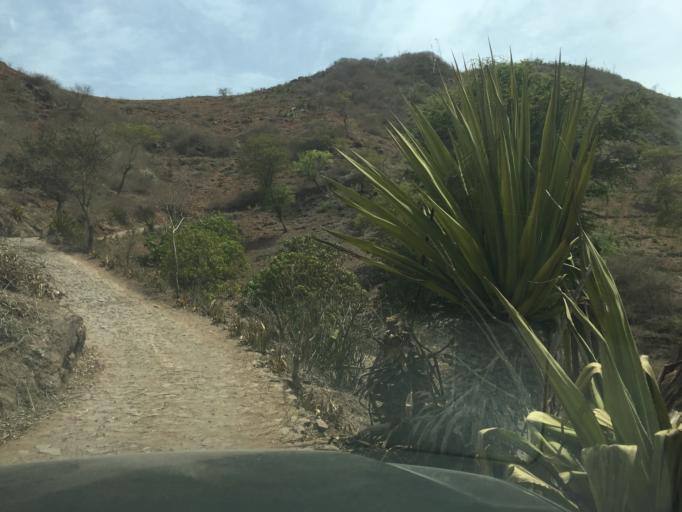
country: CV
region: Sao Salvador do Mundo
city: Picos
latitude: 15.1131
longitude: -23.6488
